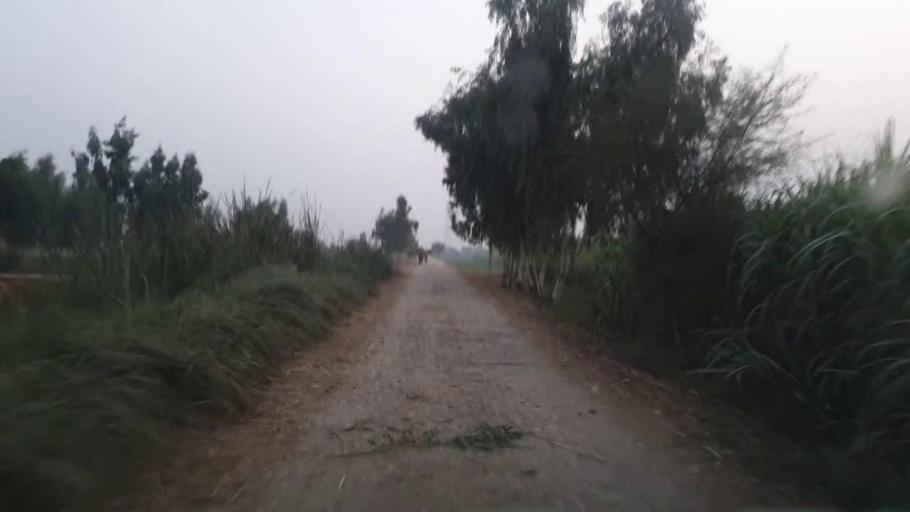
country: PK
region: Sindh
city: Karaundi
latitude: 26.9272
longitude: 68.4299
